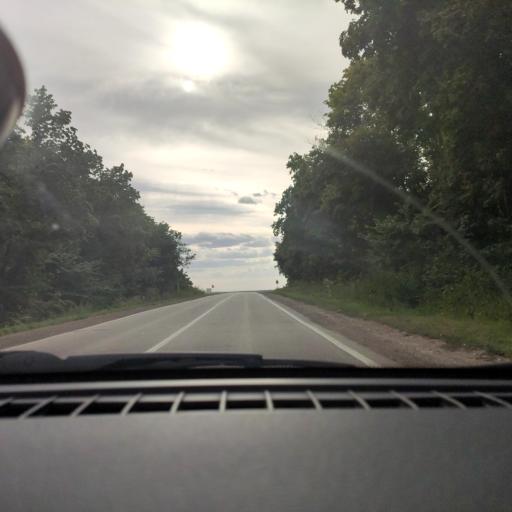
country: RU
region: Samara
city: Kinel'
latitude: 53.4415
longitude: 50.6335
